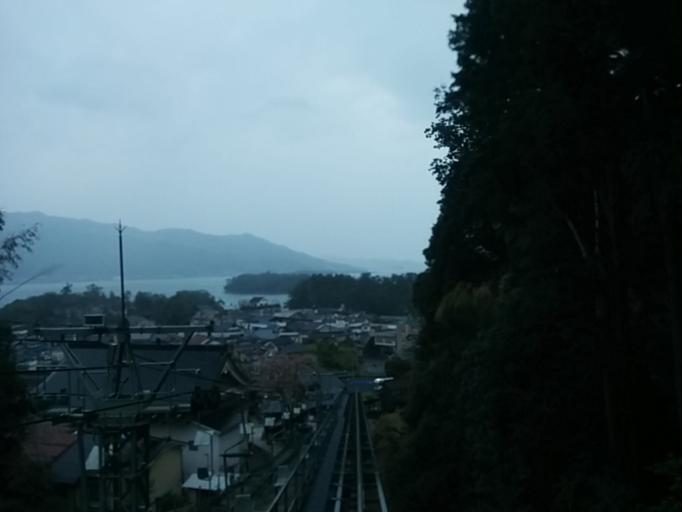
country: JP
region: Kyoto
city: Miyazu
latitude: 35.5551
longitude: 135.1835
